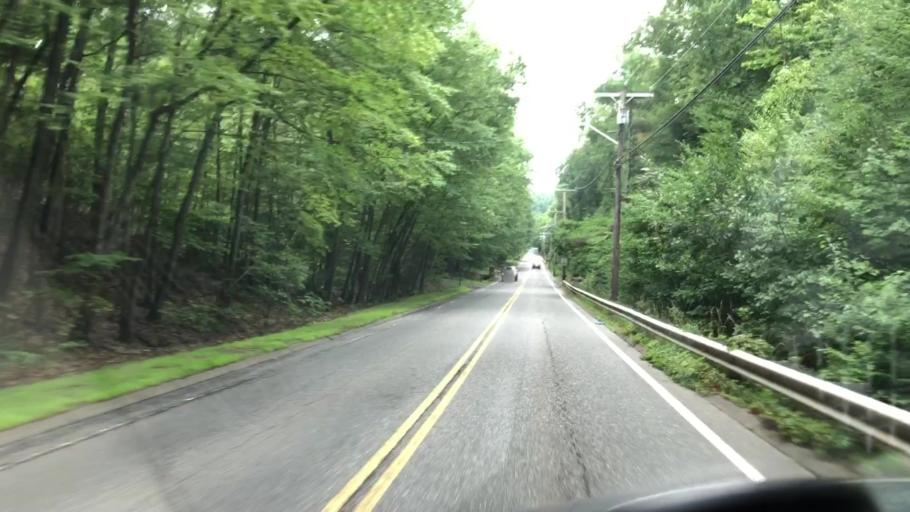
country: US
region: Massachusetts
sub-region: Hampshire County
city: Easthampton
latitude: 42.2154
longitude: -72.6693
